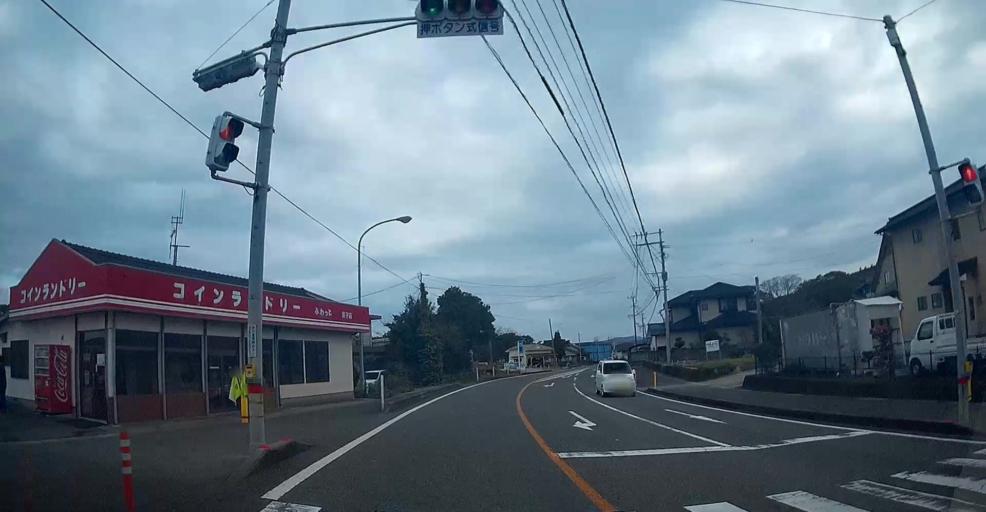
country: JP
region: Kumamoto
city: Hondo
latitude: 32.4771
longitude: 130.2612
